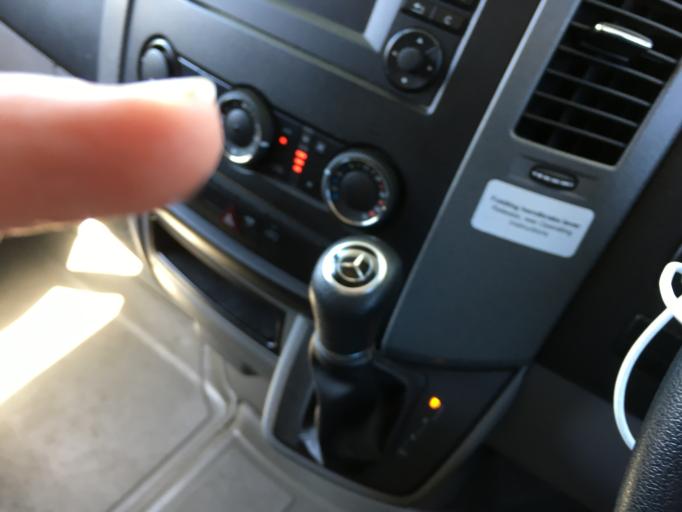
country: NZ
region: West Coast
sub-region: Grey District
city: Greymouth
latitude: -42.5344
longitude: 171.1822
